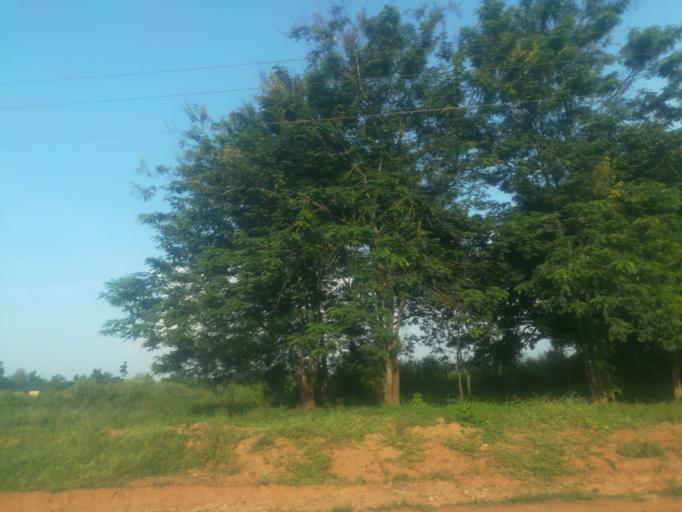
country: NG
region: Oyo
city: Moniya
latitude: 7.5581
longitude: 3.8879
